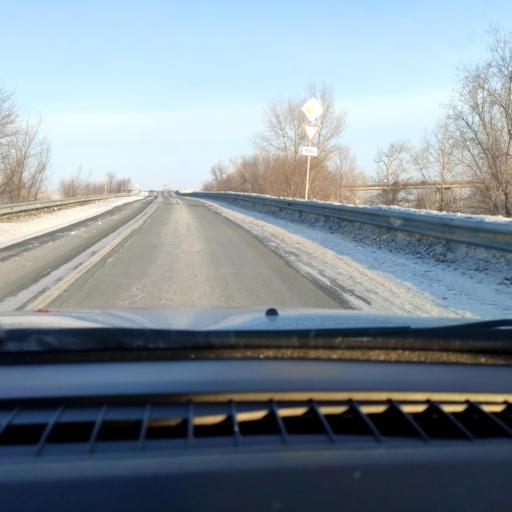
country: RU
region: Samara
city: Kinel'
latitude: 53.1864
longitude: 50.5134
